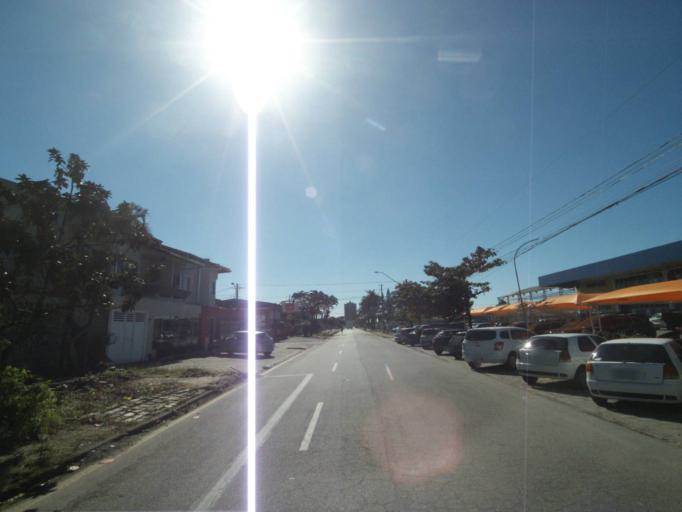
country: BR
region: Parana
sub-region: Paranagua
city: Paranagua
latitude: -25.5268
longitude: -48.5225
